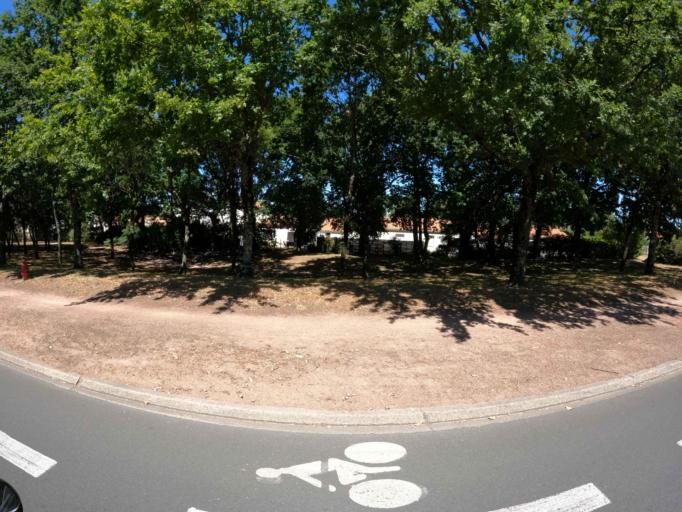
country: FR
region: Pays de la Loire
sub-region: Departement de la Vendee
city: Challans
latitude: 46.8359
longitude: -1.8764
